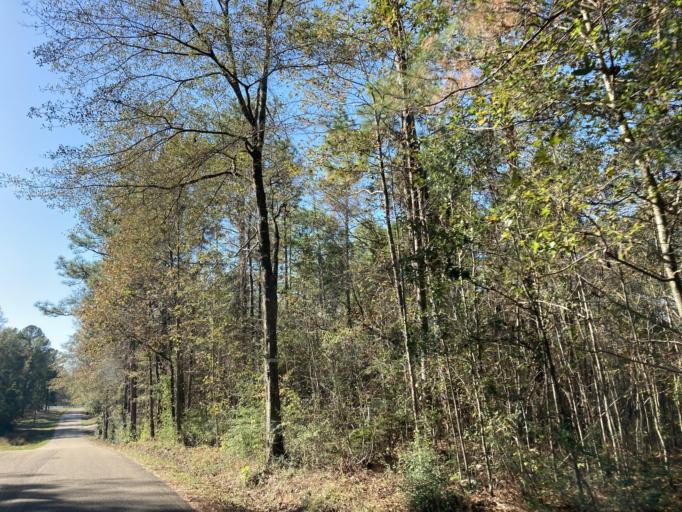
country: US
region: Mississippi
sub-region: Lamar County
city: Sumrall
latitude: 31.3406
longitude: -89.5050
